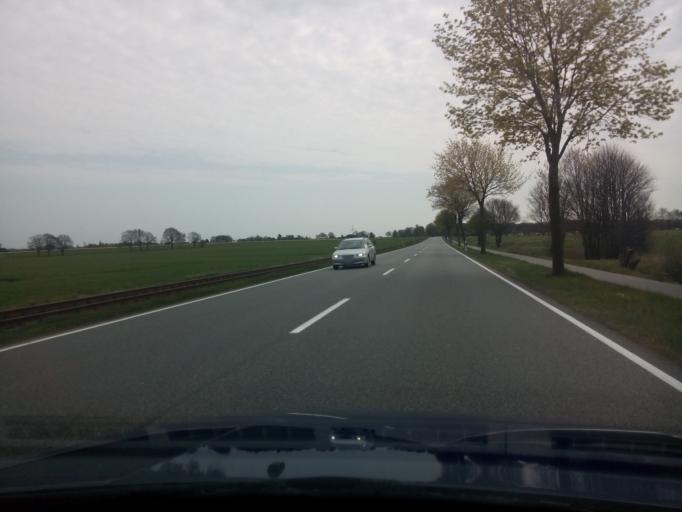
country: DE
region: Lower Saxony
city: Syke
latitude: 52.8940
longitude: 8.8471
